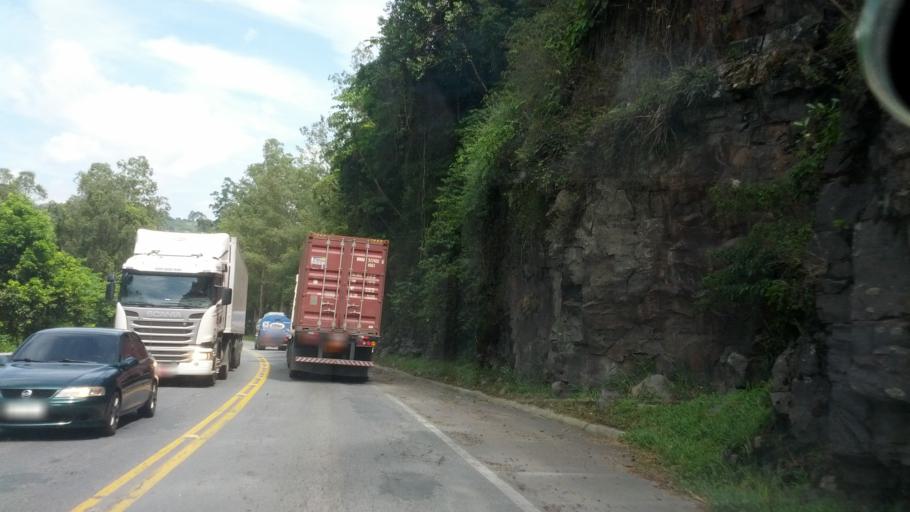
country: BR
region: Santa Catarina
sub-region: Ibirama
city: Ibirama
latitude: -27.0822
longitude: -49.5070
